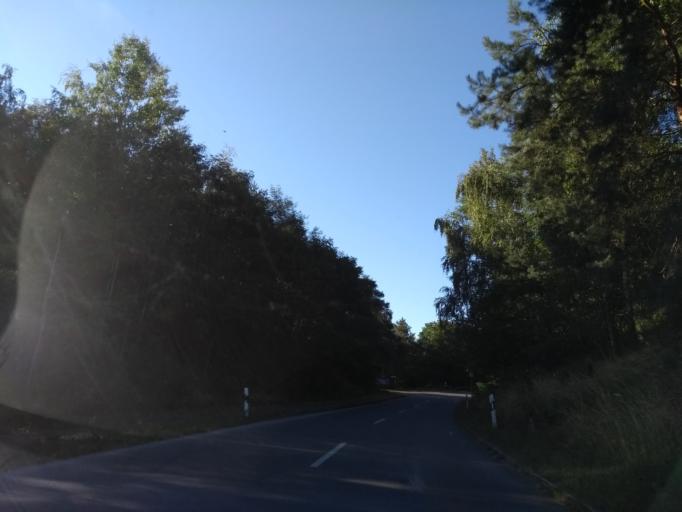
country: DE
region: Brandenburg
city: Lubbenau
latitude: 51.8416
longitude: 13.9506
